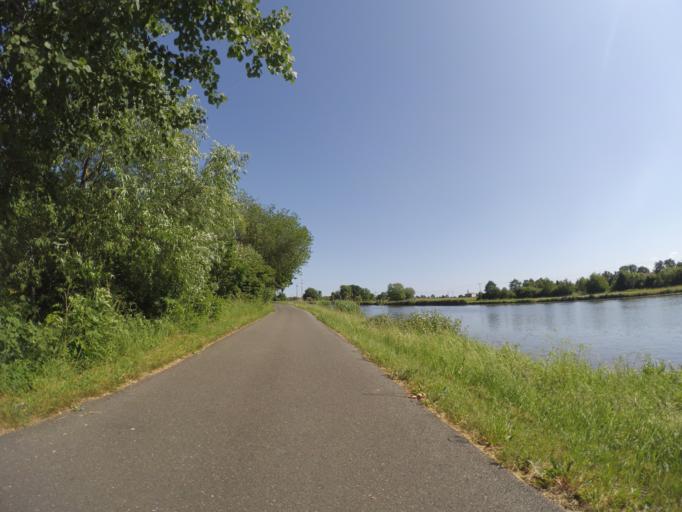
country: CZ
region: Central Bohemia
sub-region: Okres Nymburk
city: Nymburk
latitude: 50.1703
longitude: 15.0779
